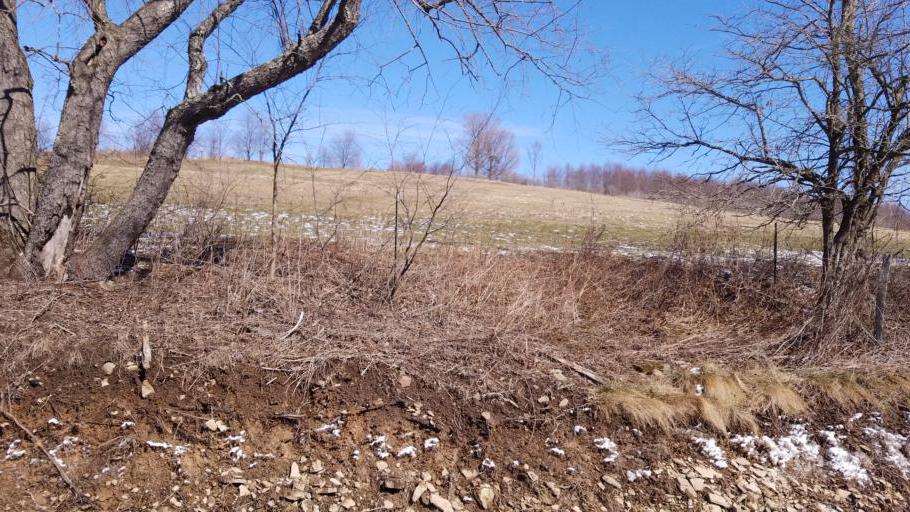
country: US
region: Pennsylvania
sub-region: Tioga County
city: Westfield
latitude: 41.9224
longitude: -77.7563
